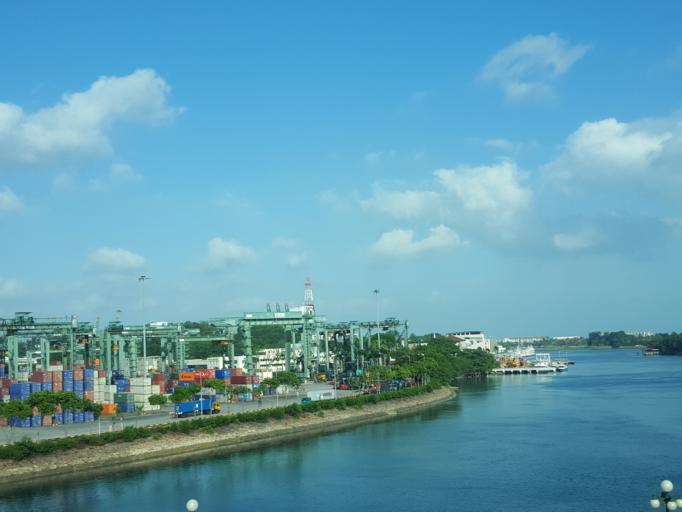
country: SG
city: Singapore
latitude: 1.2583
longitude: 103.8237
